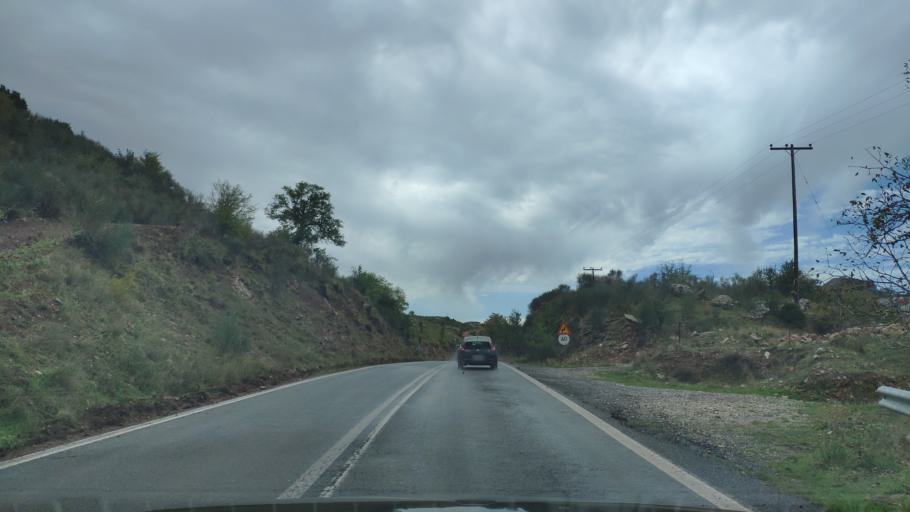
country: GR
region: Peloponnese
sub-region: Nomos Arkadias
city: Dimitsana
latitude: 37.6030
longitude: 22.0402
